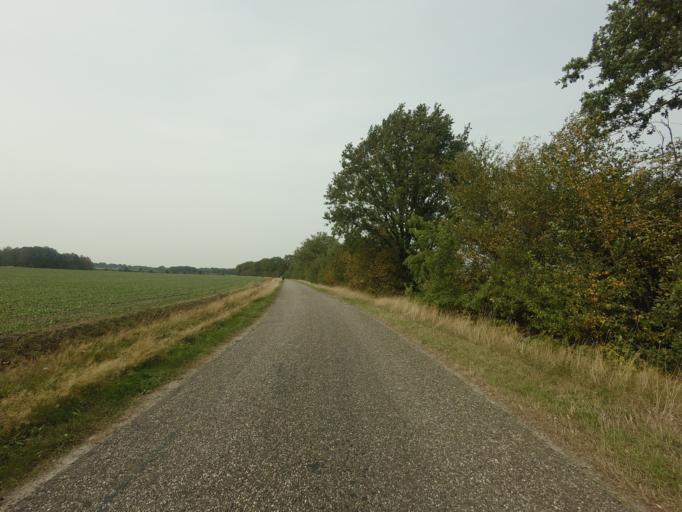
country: NL
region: Drenthe
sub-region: Gemeente Tynaarlo
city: Vries
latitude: 53.1046
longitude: 6.5494
